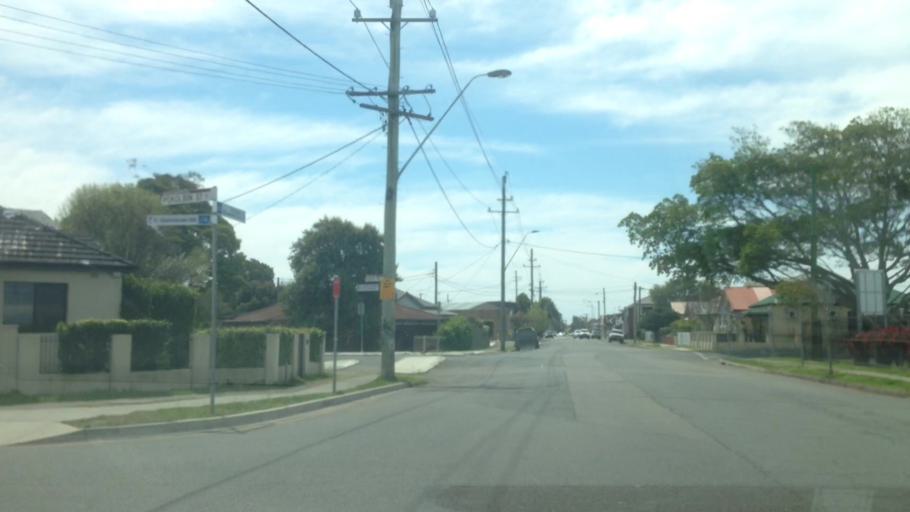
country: AU
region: New South Wales
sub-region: Newcastle
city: Broadmeadow
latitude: -32.9273
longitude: 151.7368
